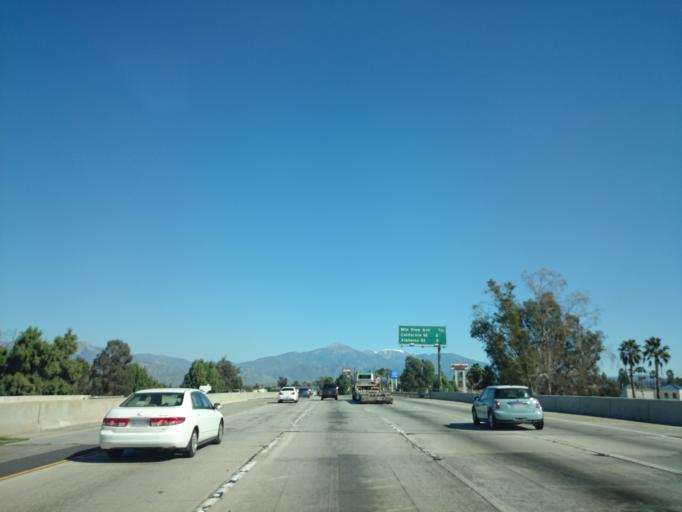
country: US
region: California
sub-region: San Bernardino County
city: Loma Linda
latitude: 34.0643
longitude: -117.2616
